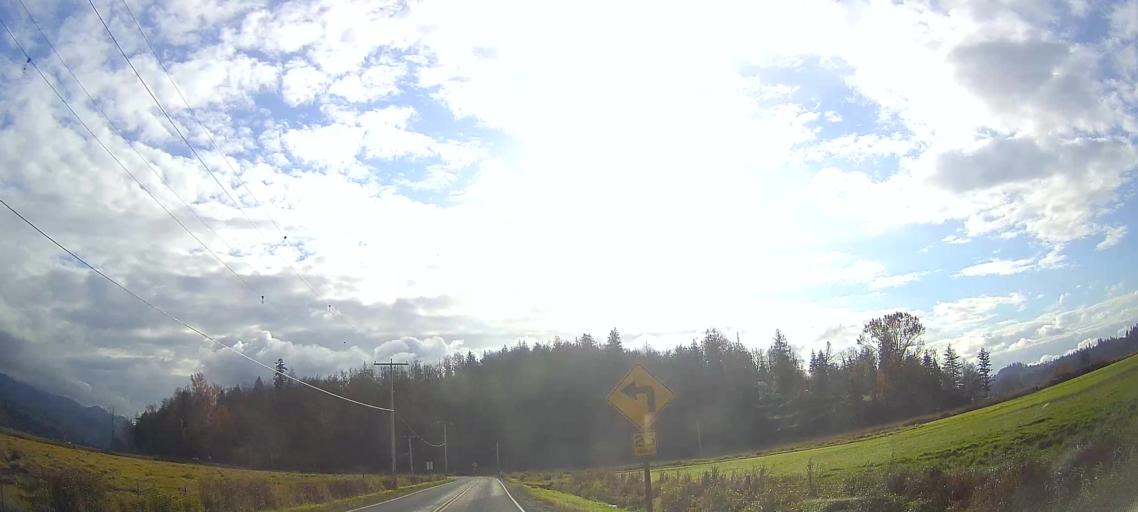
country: US
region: Washington
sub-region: Skagit County
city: Clear Lake
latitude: 48.4508
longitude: -122.2260
